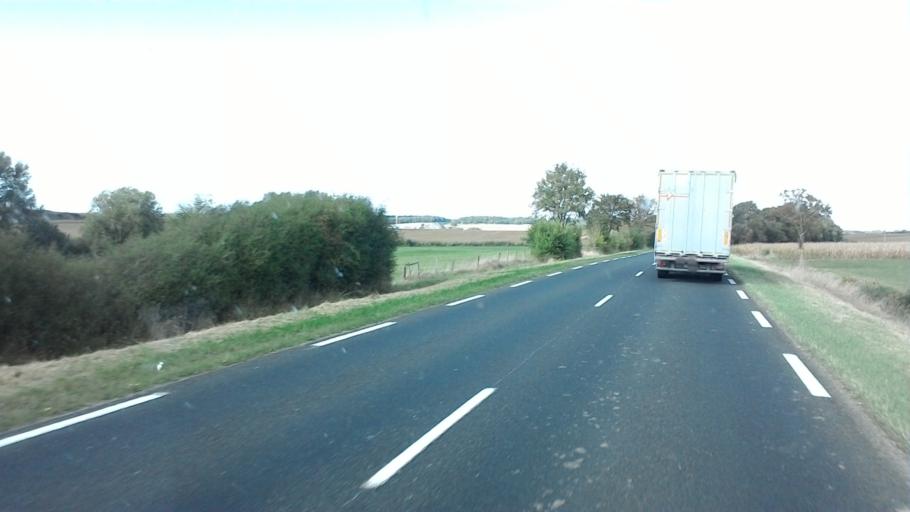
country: FR
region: Lorraine
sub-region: Departement de Meurthe-et-Moselle
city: Blenod-les-Toul
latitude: 48.6143
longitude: 5.8911
